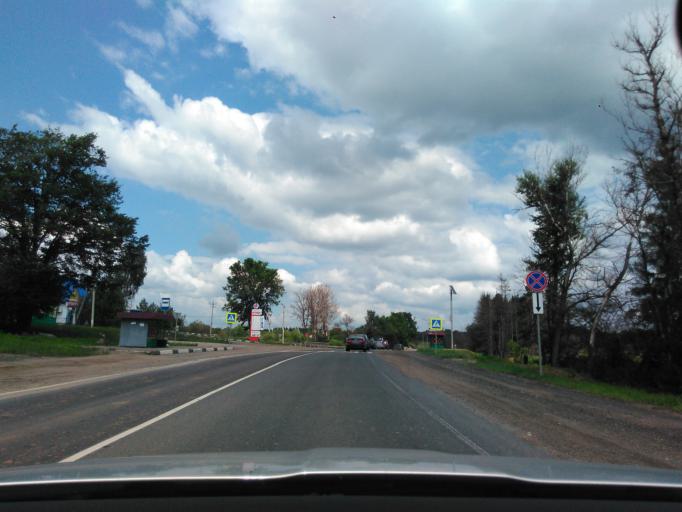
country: RU
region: Moskovskaya
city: Radumlya
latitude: 56.1069
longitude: 37.1876
